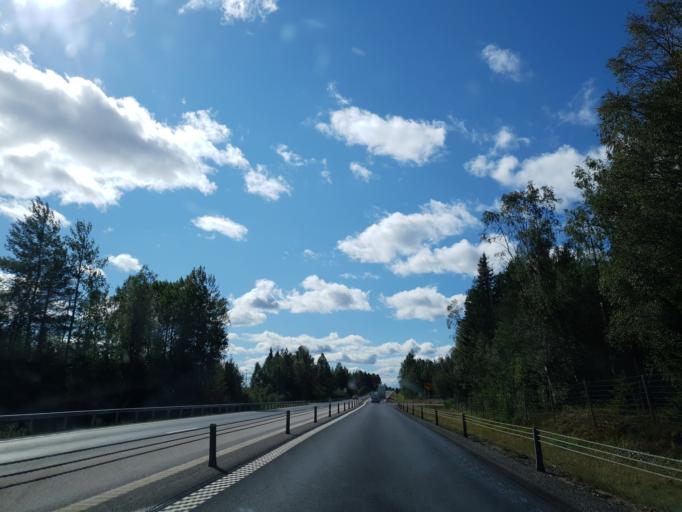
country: SE
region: Vaesterbotten
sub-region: Nordmalings Kommun
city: Nordmaling
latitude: 63.5230
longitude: 19.3819
